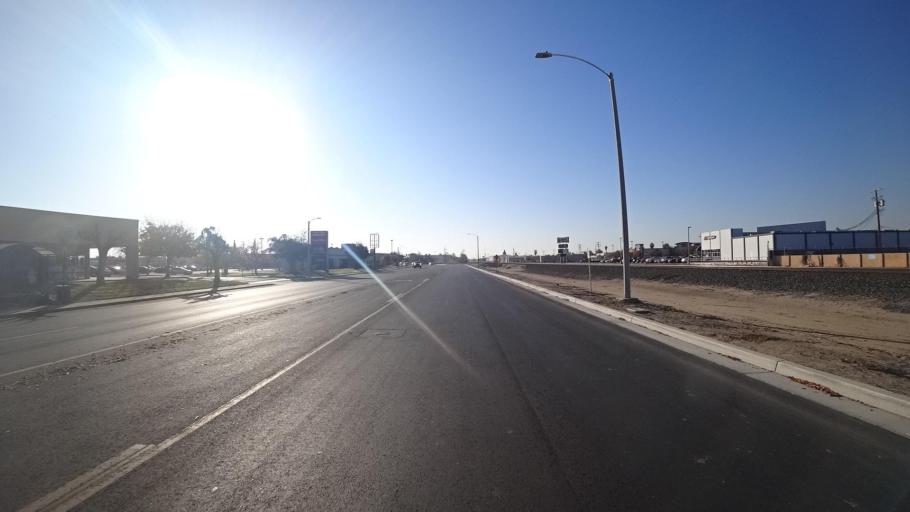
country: US
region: California
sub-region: Kern County
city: Delano
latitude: 35.7779
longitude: -119.2497
